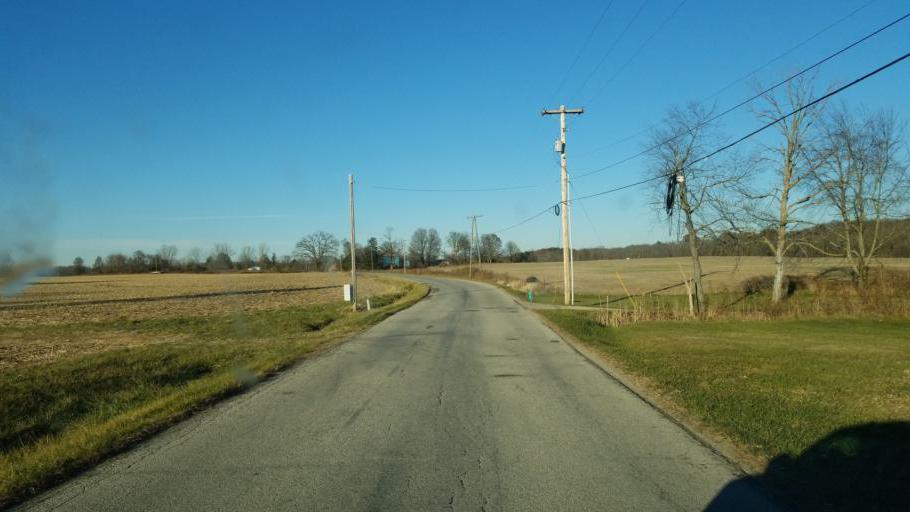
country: US
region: Ohio
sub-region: Morrow County
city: Cardington
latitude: 40.4542
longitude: -82.8421
